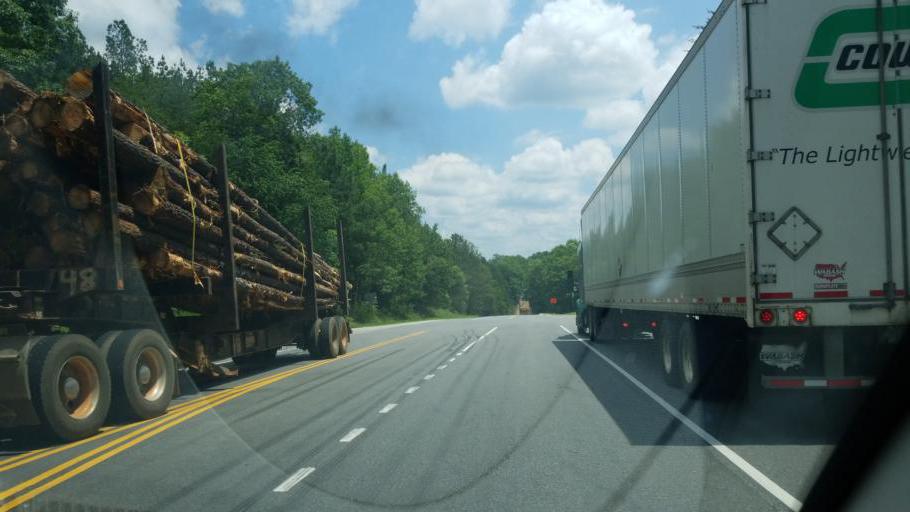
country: US
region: Virginia
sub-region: Amherst County
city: Amherst
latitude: 37.5723
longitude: -78.8976
